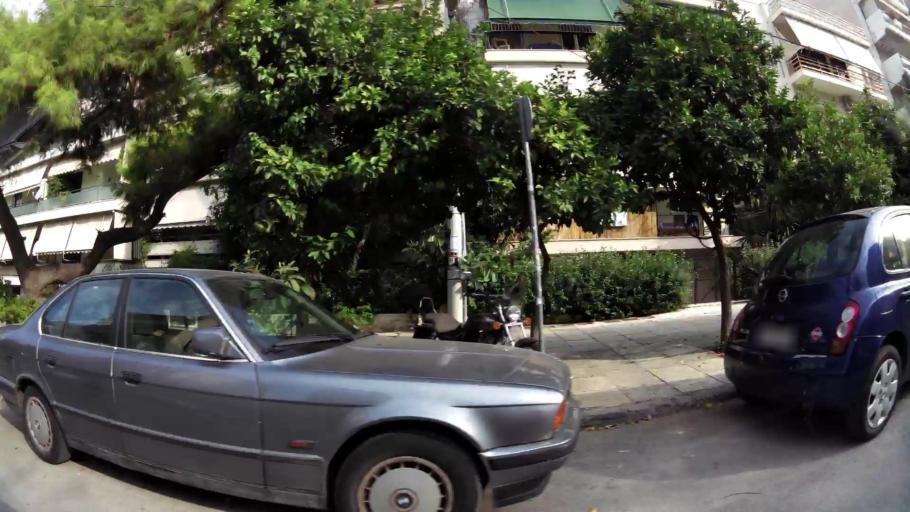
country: GR
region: Attica
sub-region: Nomarchia Athinas
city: Kallithea
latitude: 37.9432
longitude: 23.7035
